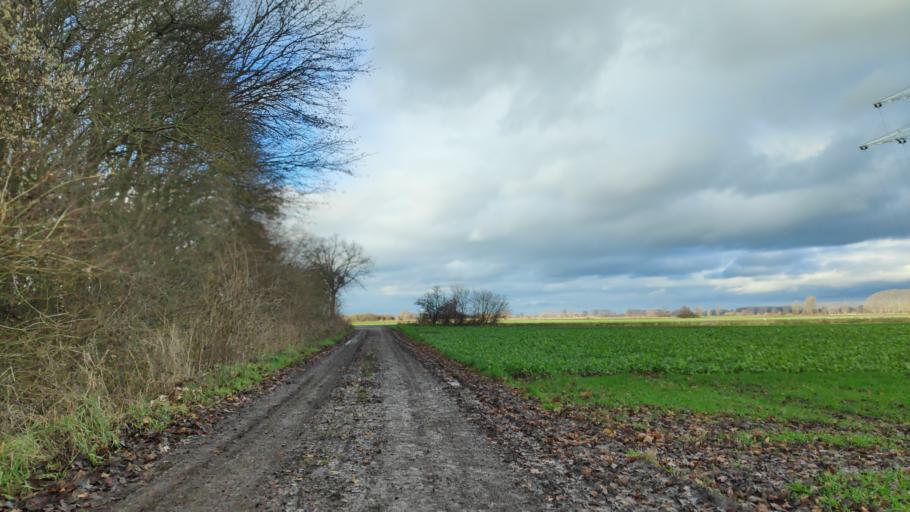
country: DE
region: North Rhine-Westphalia
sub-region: Regierungsbezirk Detmold
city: Minden
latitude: 52.2831
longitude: 8.8351
